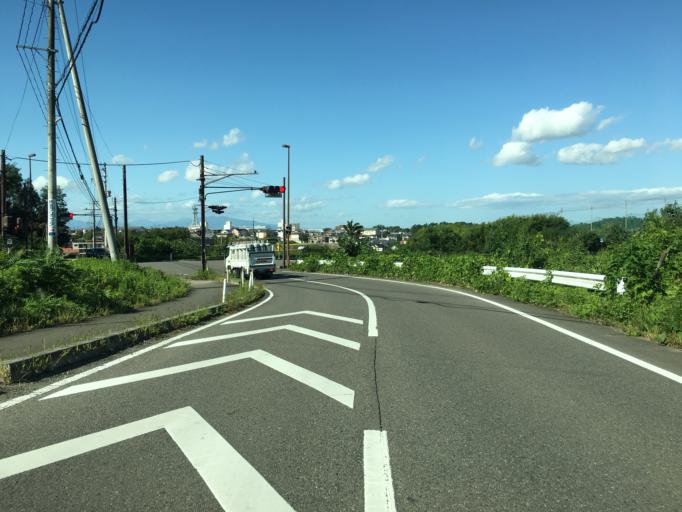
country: JP
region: Fukushima
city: Sukagawa
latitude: 37.2771
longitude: 140.3773
